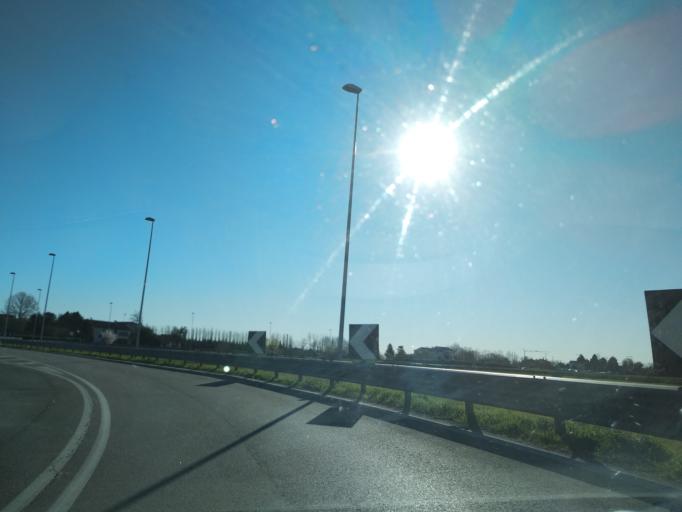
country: IT
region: Veneto
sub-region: Provincia di Vicenza
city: Grisignano di Zocco
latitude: 45.4733
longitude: 11.7058
